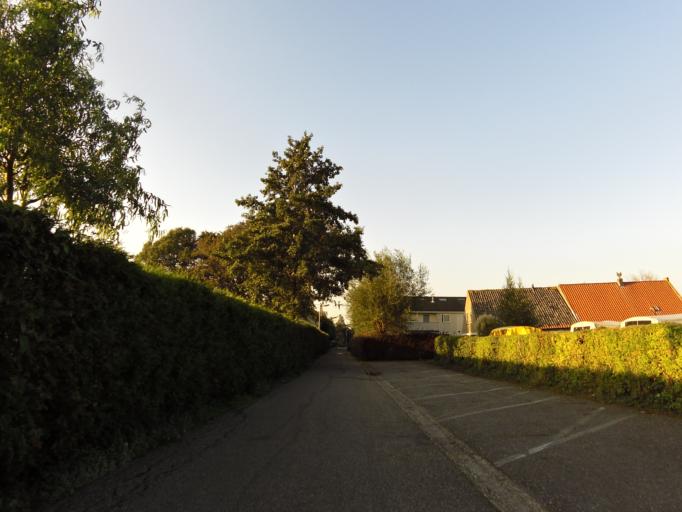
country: NL
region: South Holland
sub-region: Gemeente Alphen aan den Rijn
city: Alphen aan den Rijn
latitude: 52.1641
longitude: 4.6394
